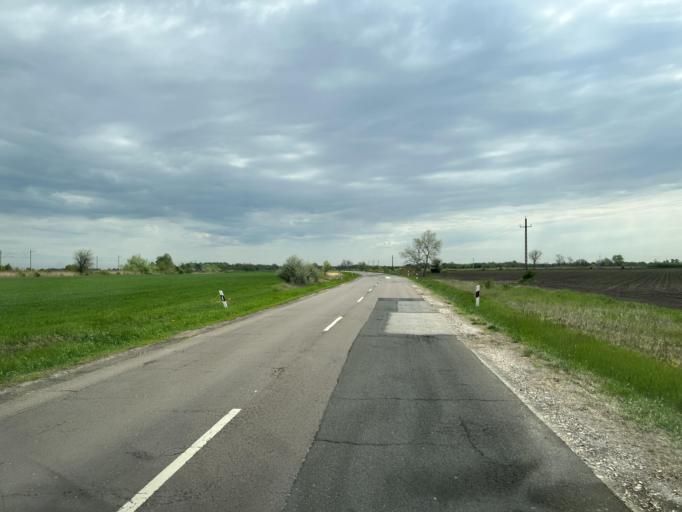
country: HU
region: Pest
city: Cegled
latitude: 47.1792
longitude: 19.8630
